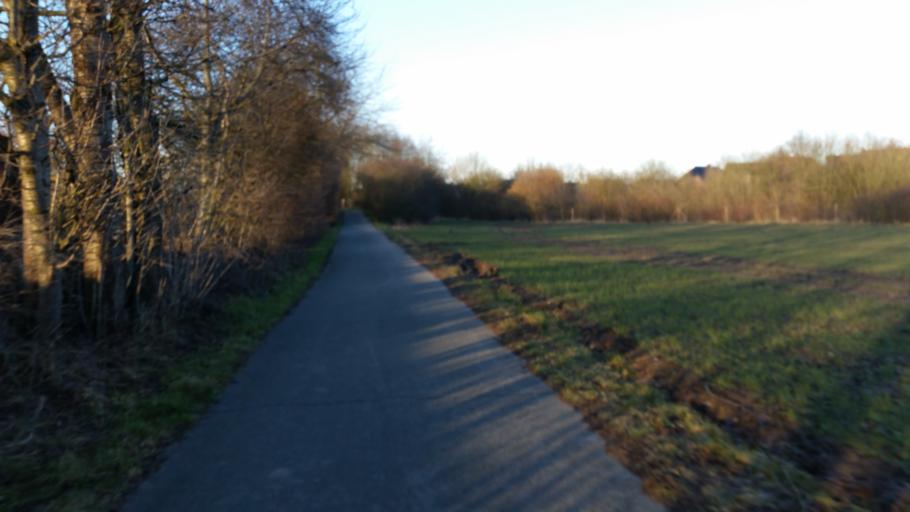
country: DE
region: North Rhine-Westphalia
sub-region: Regierungsbezirk Munster
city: Neuenkirchen
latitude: 52.2695
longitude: 7.4020
